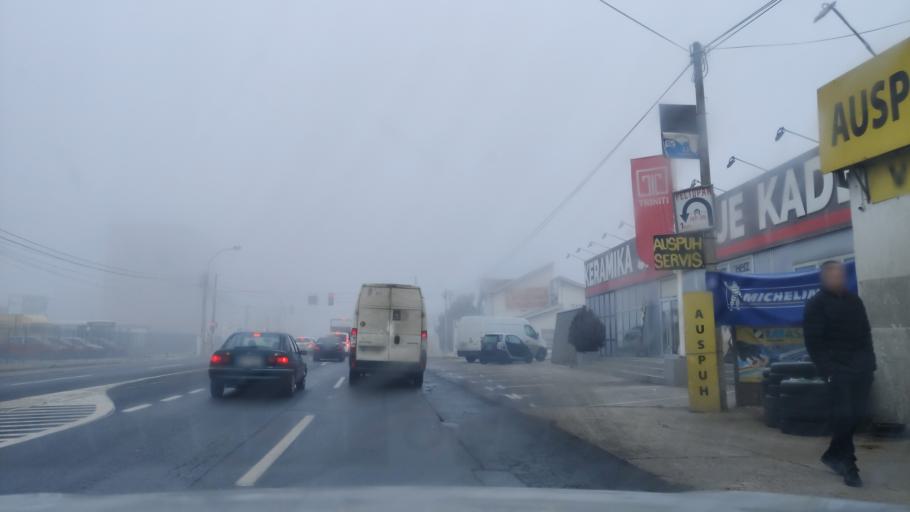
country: RS
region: Central Serbia
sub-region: Belgrade
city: Stari Grad
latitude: 44.8605
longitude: 20.4789
